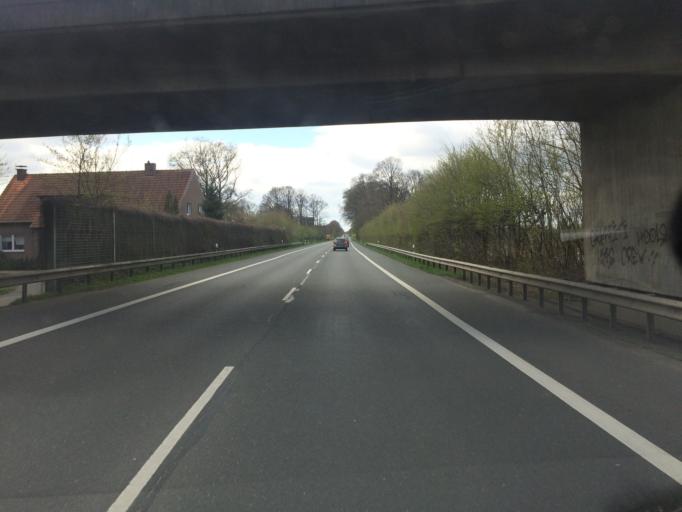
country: DE
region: North Rhine-Westphalia
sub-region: Regierungsbezirk Munster
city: Coesfeld
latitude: 51.9339
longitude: 7.1301
